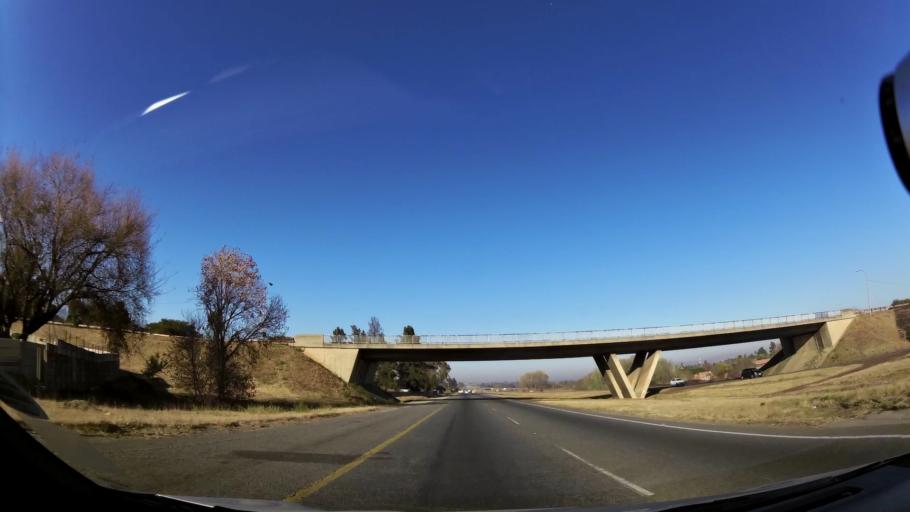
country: ZA
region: Gauteng
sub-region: Ekurhuleni Metropolitan Municipality
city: Germiston
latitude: -26.3304
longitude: 28.1112
